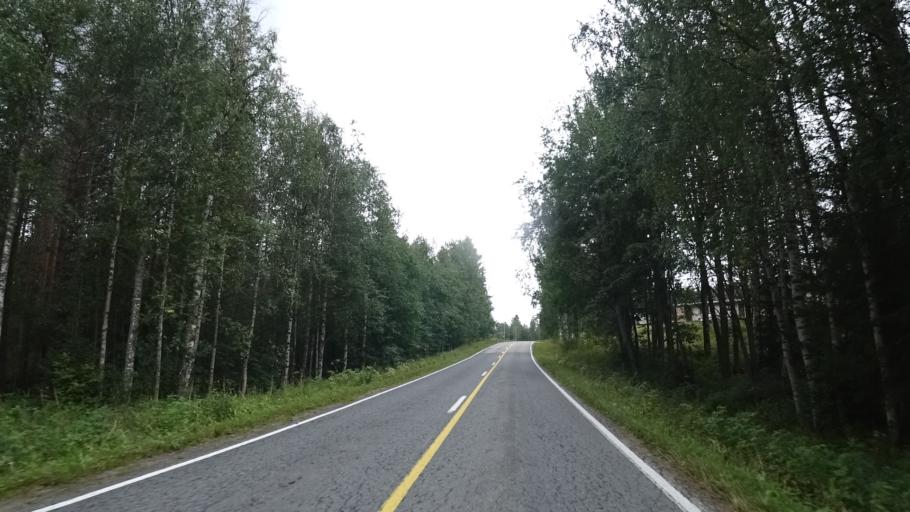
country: FI
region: North Karelia
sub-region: Joensuu
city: Ilomantsi
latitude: 62.9383
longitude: 31.2855
